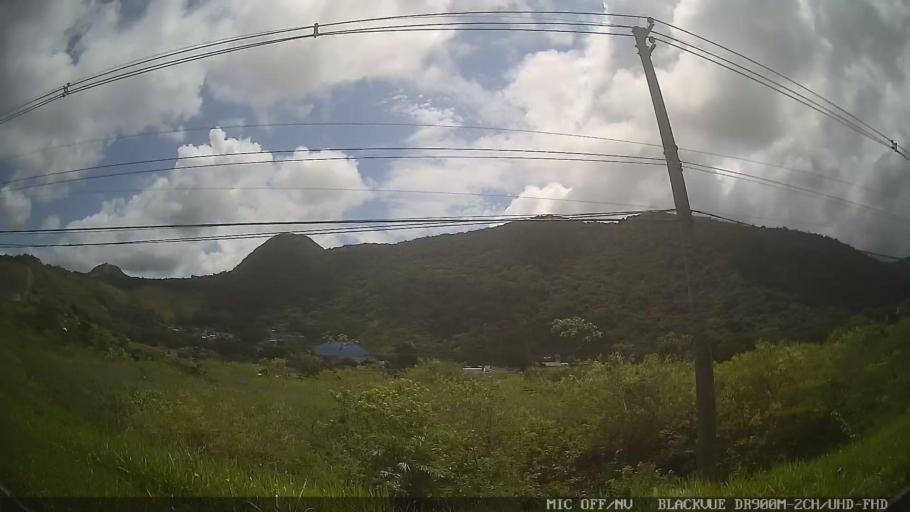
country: BR
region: Sao Paulo
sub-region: Caraguatatuba
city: Caraguatatuba
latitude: -23.6116
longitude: -45.3778
